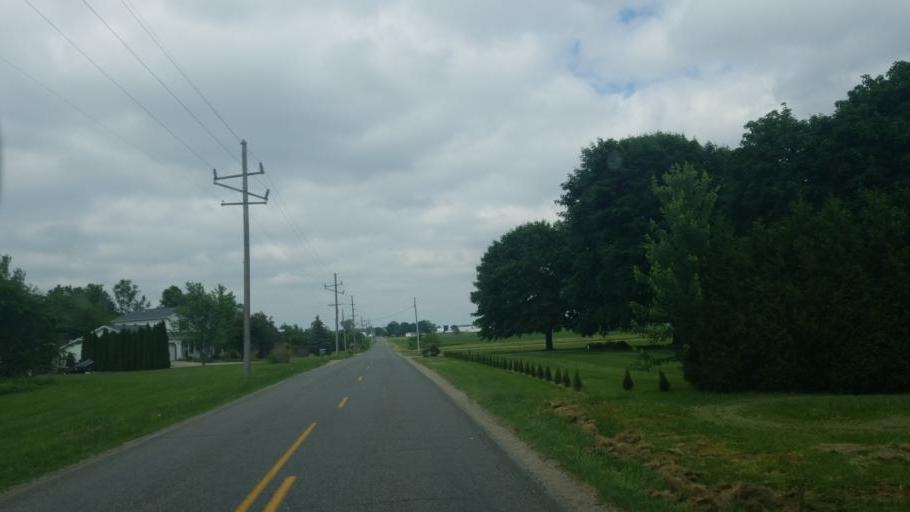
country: US
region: Indiana
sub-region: Elkhart County
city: Wakarusa
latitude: 41.4851
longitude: -86.0382
